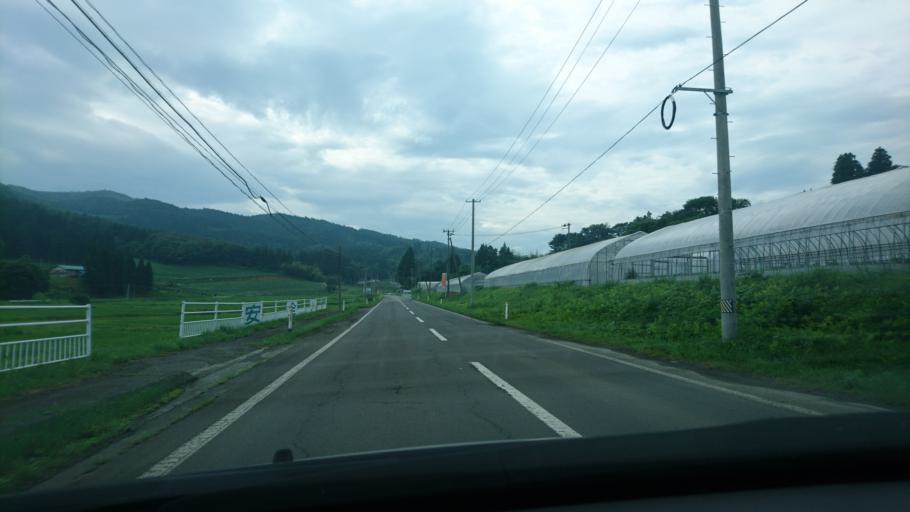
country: JP
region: Iwate
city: Ichinoseki
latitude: 38.9268
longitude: 141.4202
